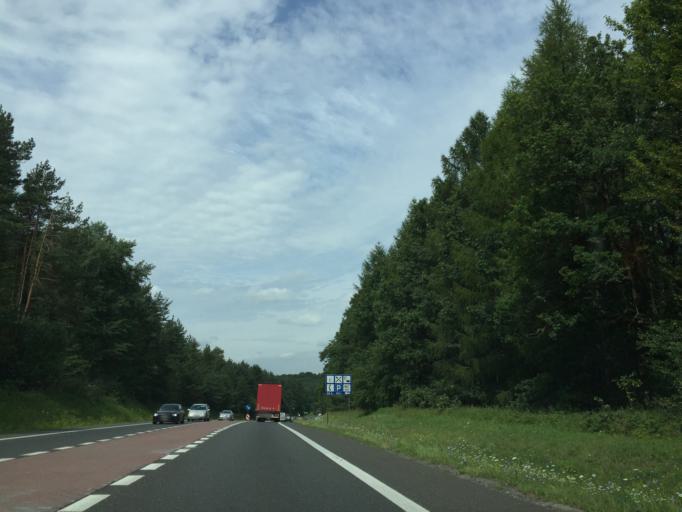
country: PL
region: Lesser Poland Voivodeship
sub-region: Powiat olkuski
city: Osiek
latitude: 50.2574
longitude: 19.6344
